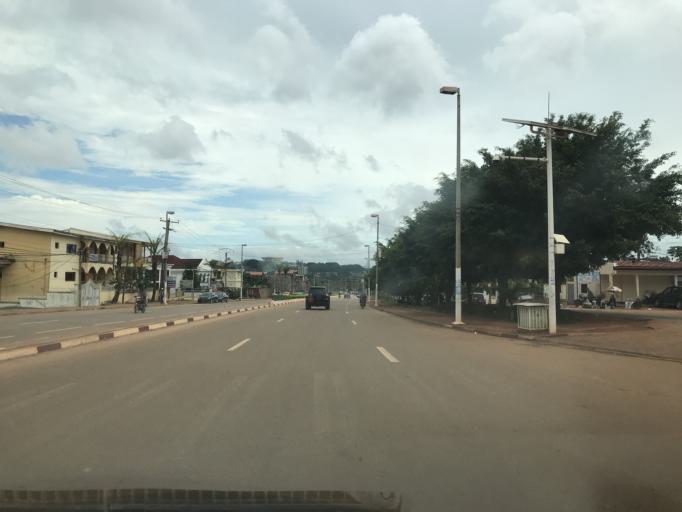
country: CM
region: Centre
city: Yaounde
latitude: 3.8951
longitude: 11.5011
